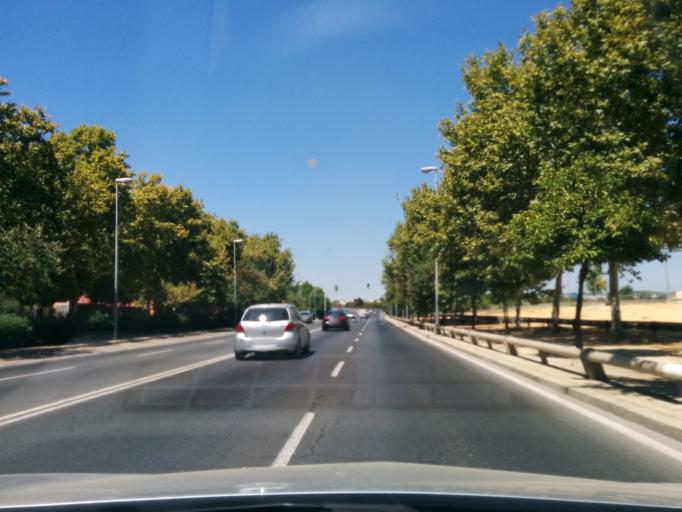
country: ES
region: Andalusia
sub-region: Provincia de Sevilla
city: San Juan de Aznalfarache
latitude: 37.3696
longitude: -6.0095
